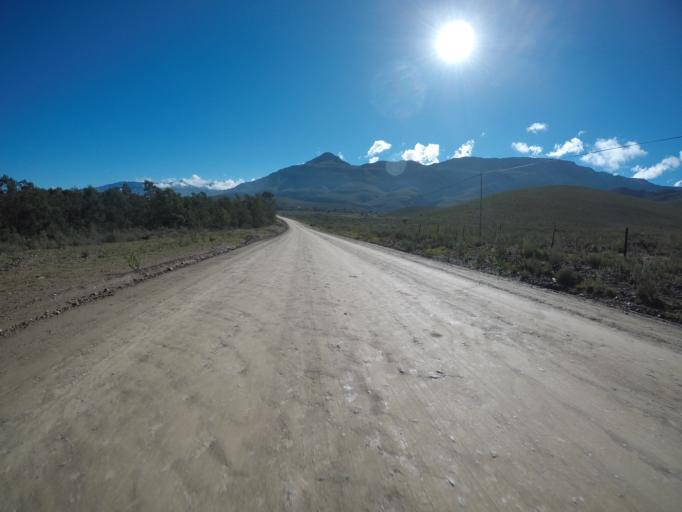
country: ZA
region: Western Cape
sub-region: Overberg District Municipality
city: Caledon
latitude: -34.0595
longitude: 19.6220
